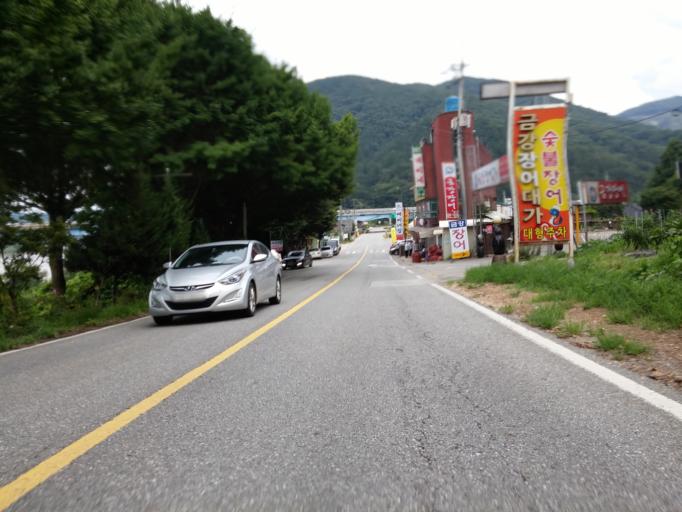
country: KR
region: Chungcheongnam-do
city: Gongju
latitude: 36.4346
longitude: 127.2089
